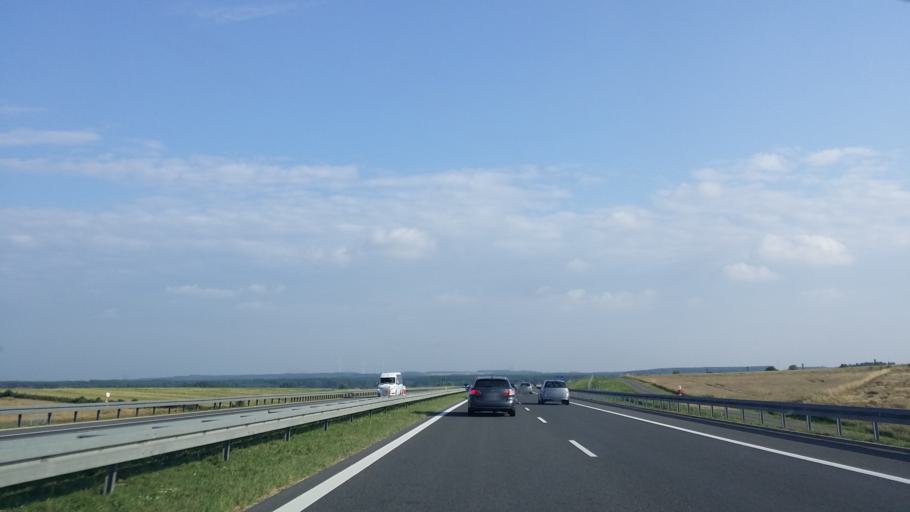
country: PL
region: Lubusz
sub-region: Powiat miedzyrzecki
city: Miedzyrzecz
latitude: 52.3552
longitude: 15.5541
